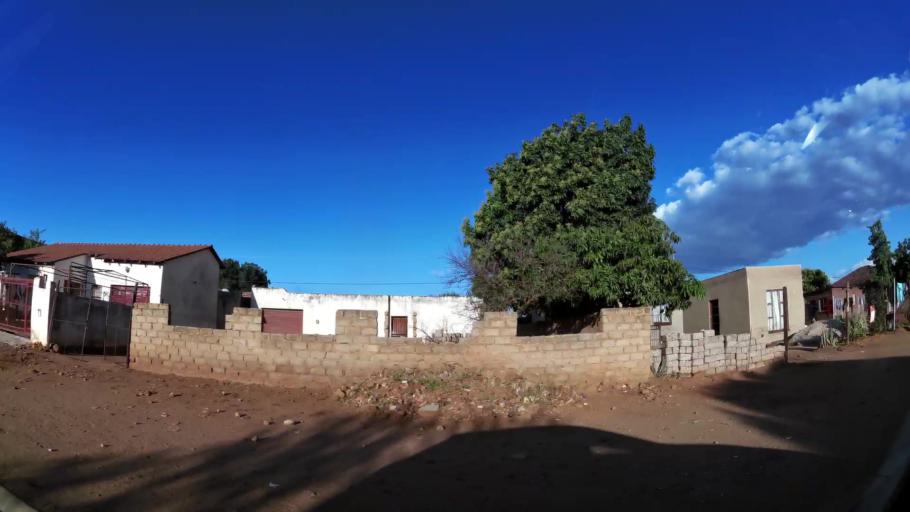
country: ZA
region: Limpopo
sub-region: Waterberg District Municipality
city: Mokopane
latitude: -24.1483
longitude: 28.9979
